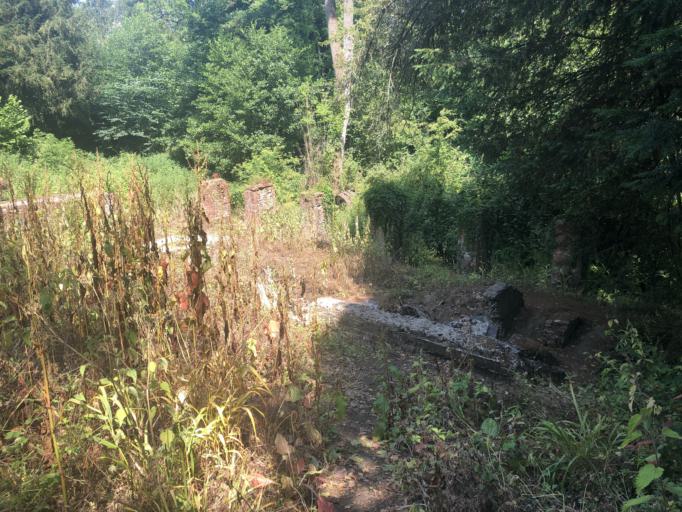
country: GB
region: England
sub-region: Surrey
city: Chilworth
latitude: 51.2172
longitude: -0.5298
